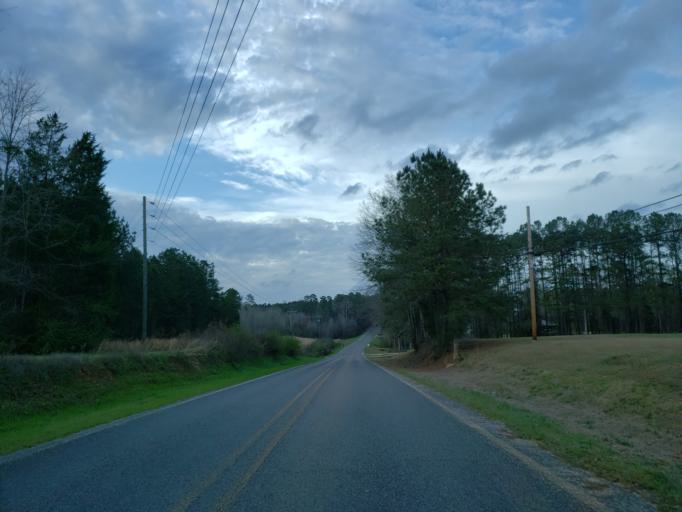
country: US
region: Mississippi
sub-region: Clarke County
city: Stonewall
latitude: 32.2188
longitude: -88.6993
